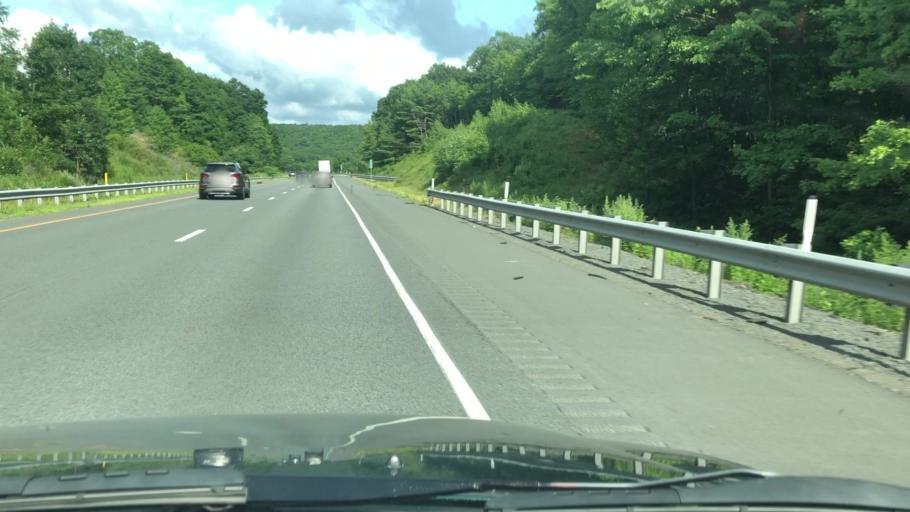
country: US
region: Pennsylvania
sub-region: Pike County
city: Milford
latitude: 41.3431
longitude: -74.8036
